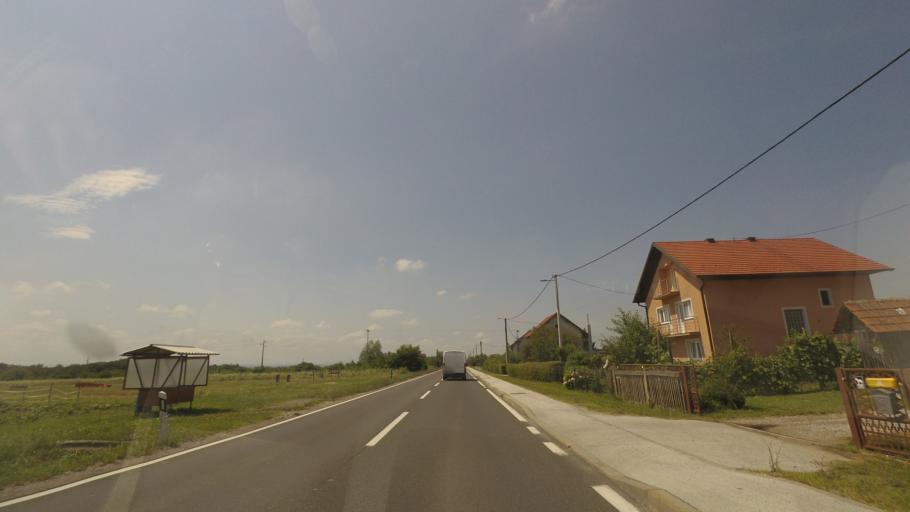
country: HR
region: Grad Zagreb
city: Horvati
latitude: 45.7119
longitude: 15.7772
